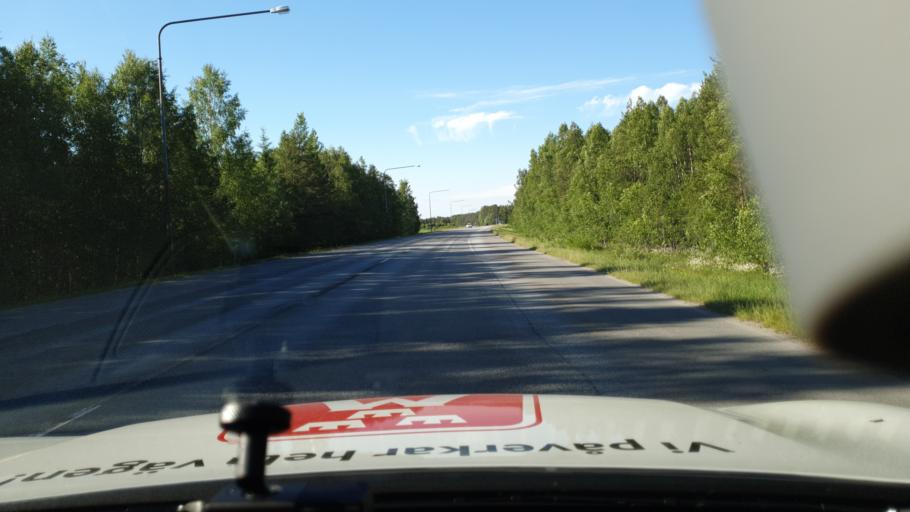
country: SE
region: Vaesterbotten
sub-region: Umea Kommun
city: Roback
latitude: 63.7811
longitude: 20.2037
